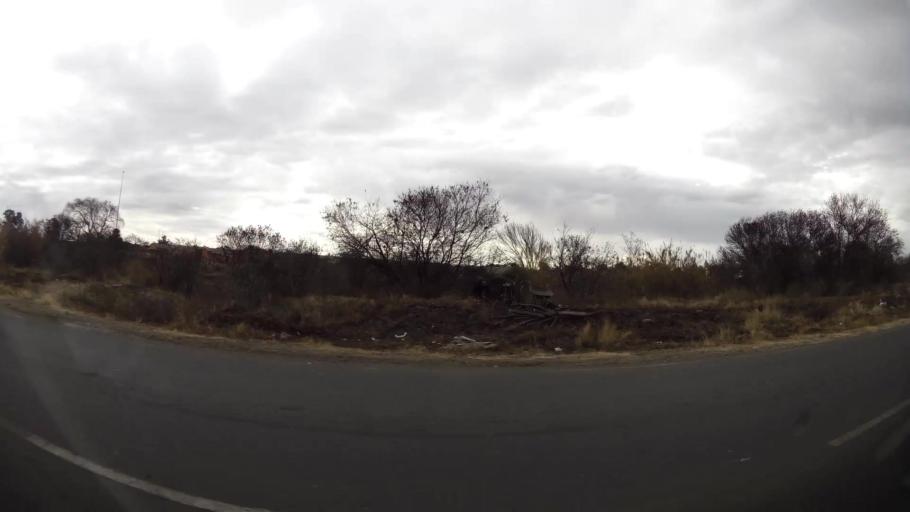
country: ZA
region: Orange Free State
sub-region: Fezile Dabi District Municipality
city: Kroonstad
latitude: -27.6500
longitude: 27.2274
